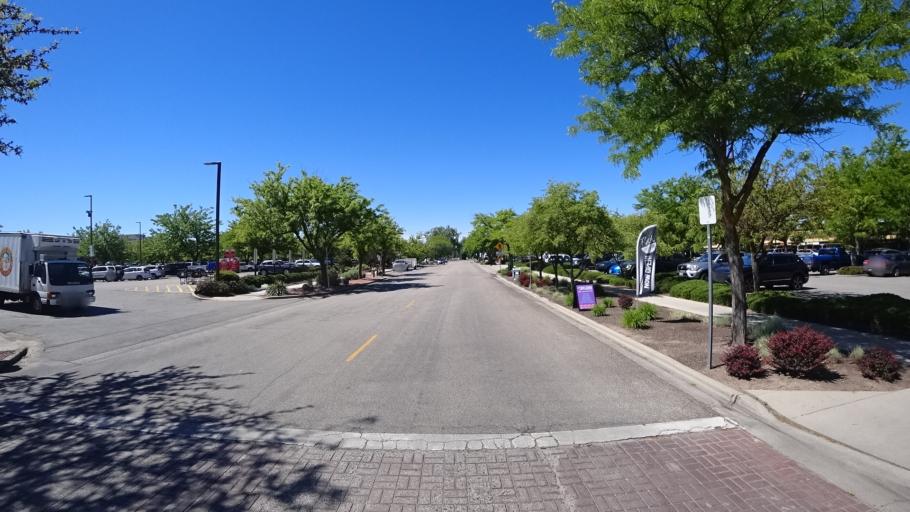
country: US
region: Idaho
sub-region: Ada County
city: Boise
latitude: 43.6252
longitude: -116.2101
